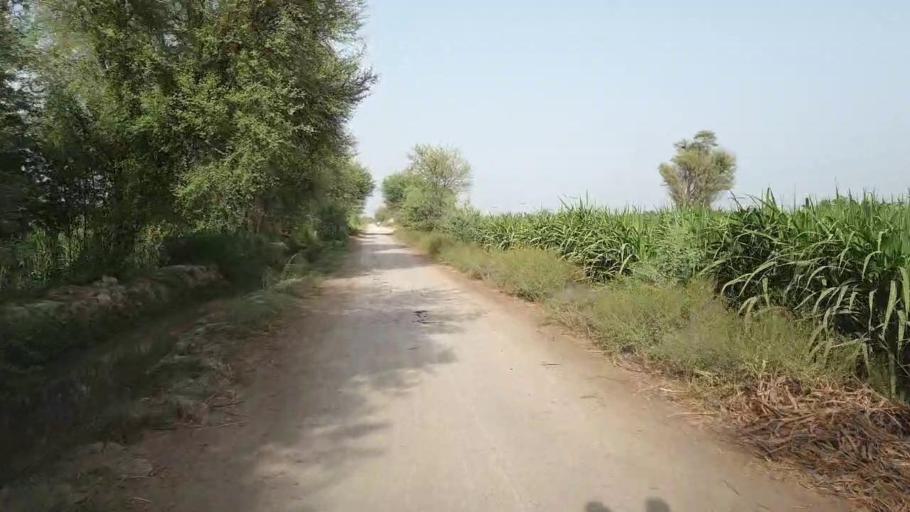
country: PK
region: Sindh
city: Daur
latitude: 26.3408
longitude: 68.1917
